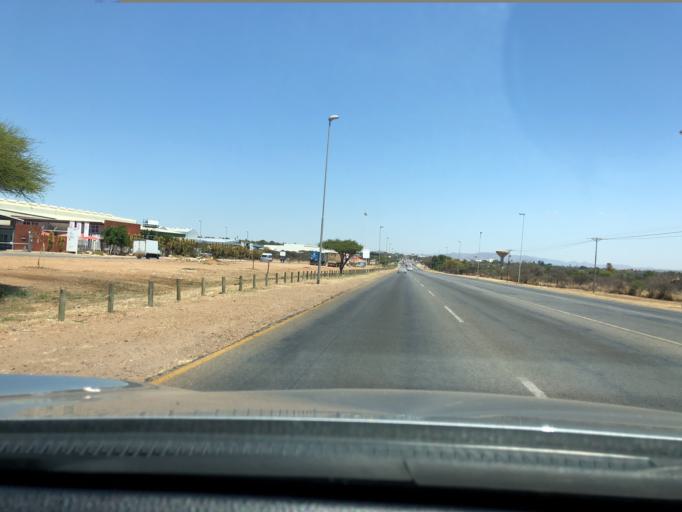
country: ZA
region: Limpopo
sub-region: Capricorn District Municipality
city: Polokwane
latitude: -23.8650
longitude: 29.4687
